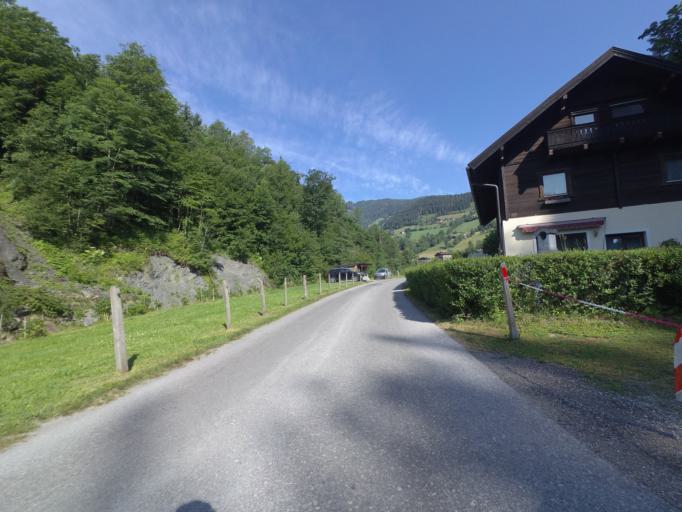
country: AT
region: Salzburg
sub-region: Politischer Bezirk Sankt Johann im Pongau
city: Sankt Veit im Pongau
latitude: 47.3301
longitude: 13.1251
